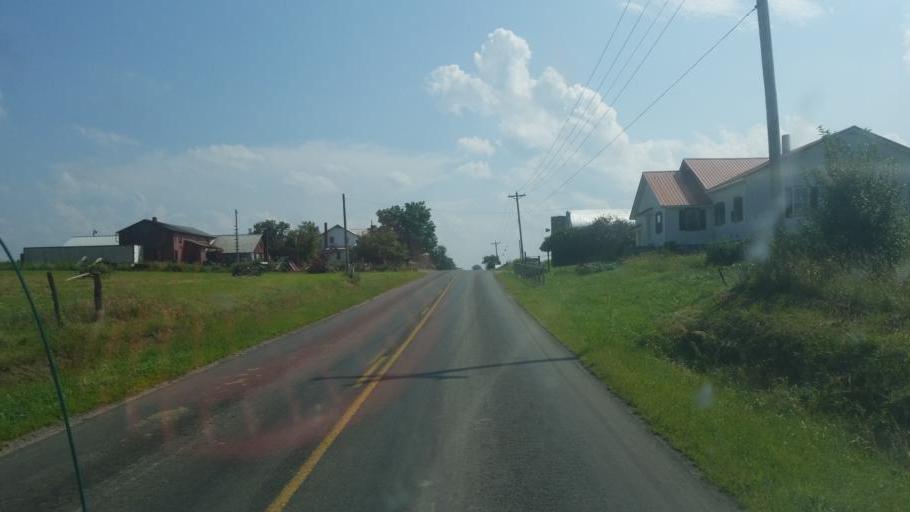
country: US
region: Ohio
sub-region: Wayne County
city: West Salem
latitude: 41.0515
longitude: -82.1630
